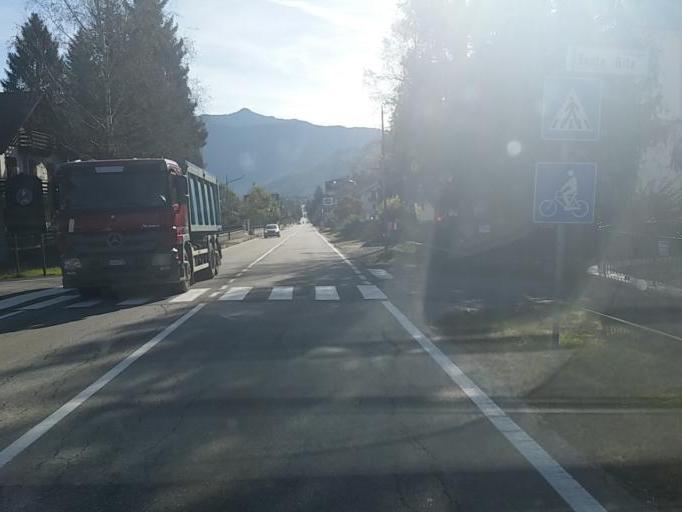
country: IT
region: Piedmont
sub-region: Provincia Verbano-Cusio-Ossola
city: Craveggia
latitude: 46.1310
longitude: 8.4847
